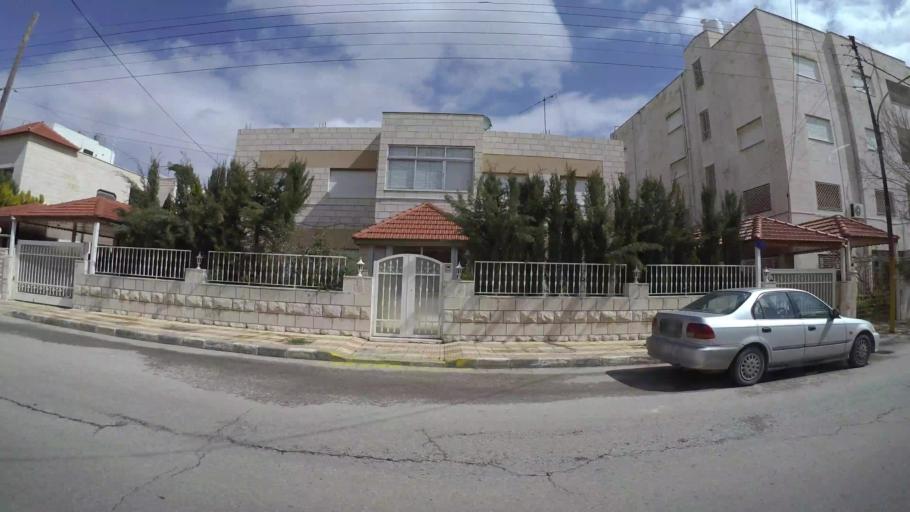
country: JO
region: Amman
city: Wadi as Sir
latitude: 31.9603
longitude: 35.8403
